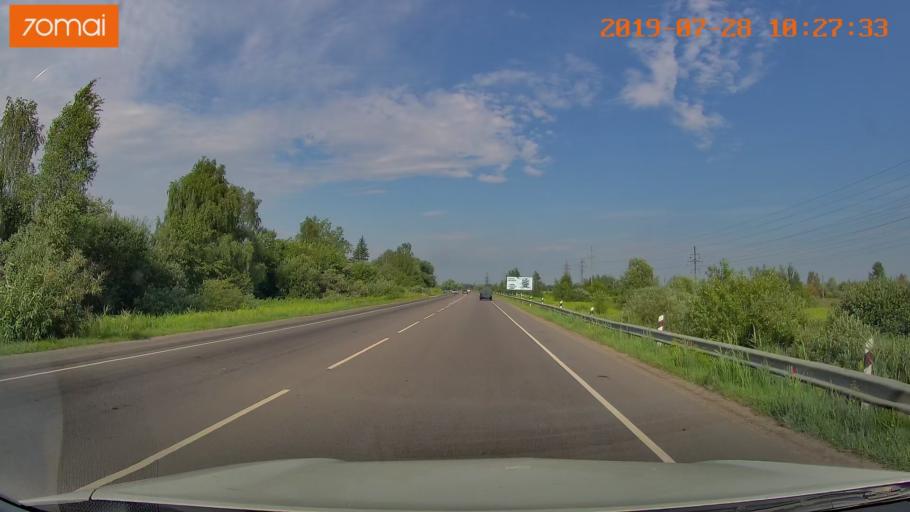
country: RU
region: Kaliningrad
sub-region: Gorod Kaliningrad
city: Kaliningrad
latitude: 54.7710
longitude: 20.5155
